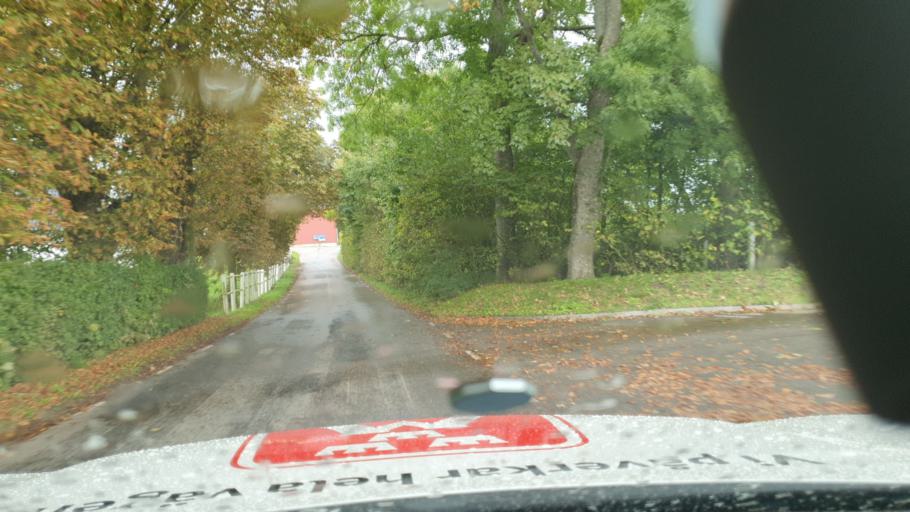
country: SE
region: Skane
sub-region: Malmo
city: Tygelsjo
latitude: 55.5238
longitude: 13.0414
